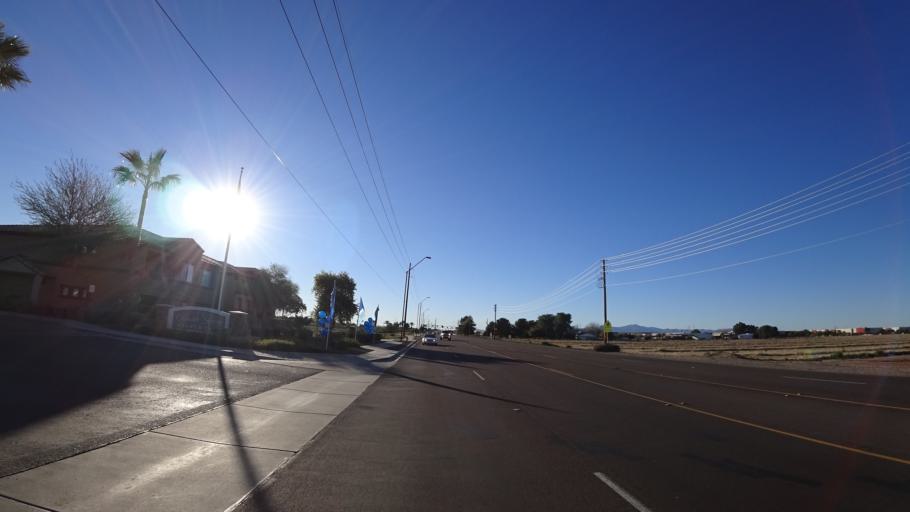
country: US
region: Arizona
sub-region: Maricopa County
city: Avondale
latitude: 33.4494
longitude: -112.3201
